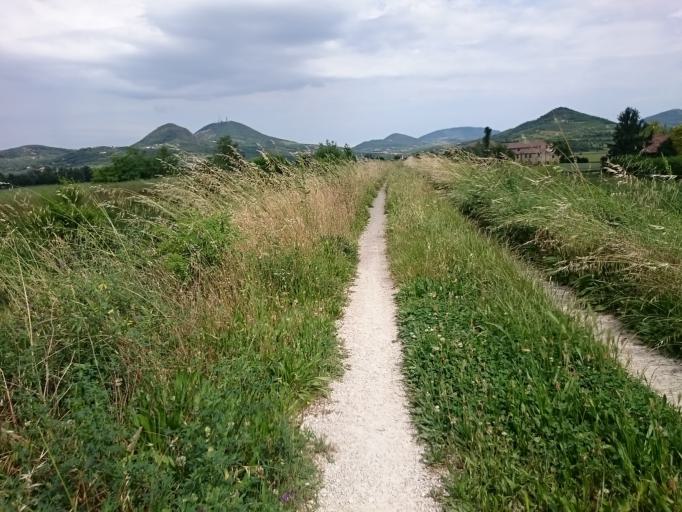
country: IT
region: Veneto
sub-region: Provincia di Padova
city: Baone
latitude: 45.2219
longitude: 11.6934
